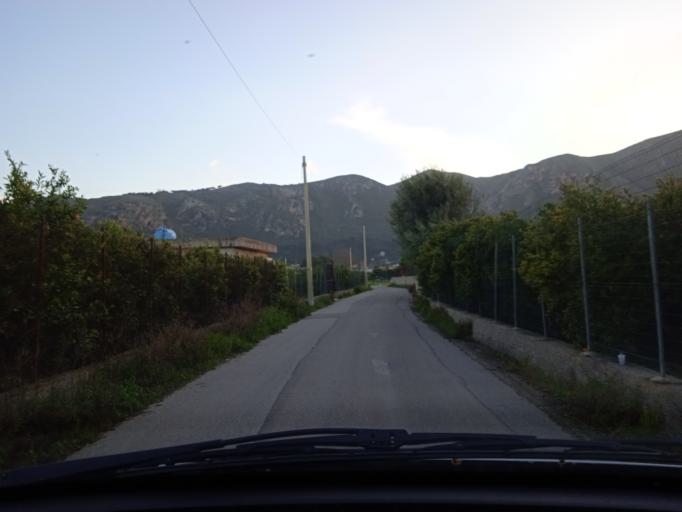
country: IT
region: Sicily
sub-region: Palermo
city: Villabate
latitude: 38.0776
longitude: 13.4274
